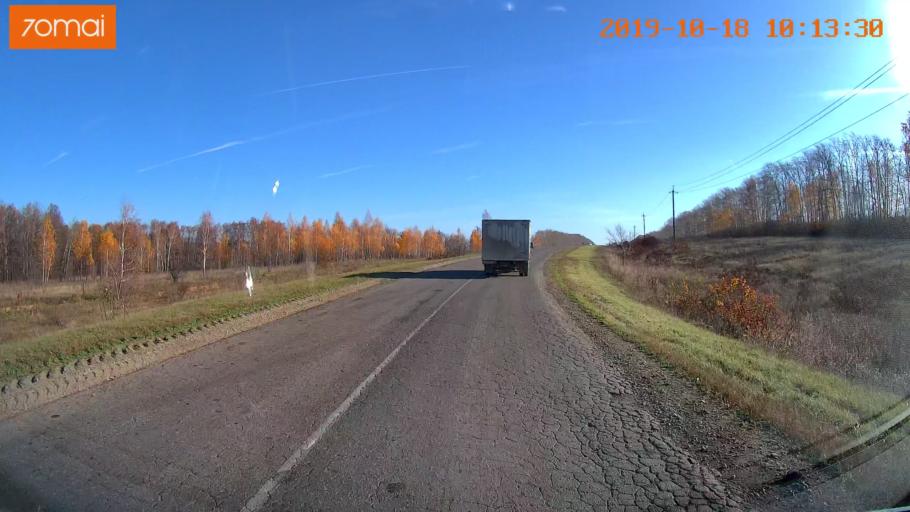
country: RU
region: Tula
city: Kurkino
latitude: 53.4022
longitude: 38.5214
